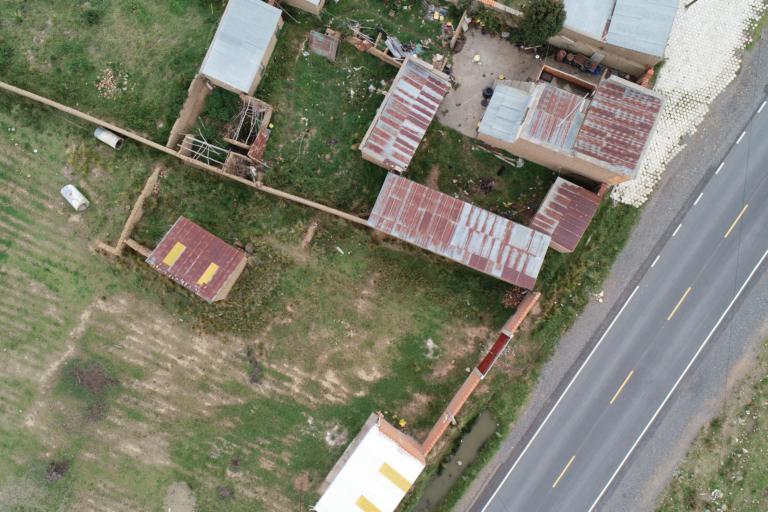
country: BO
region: La Paz
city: Huarina
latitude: -16.1858
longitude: -68.6044
